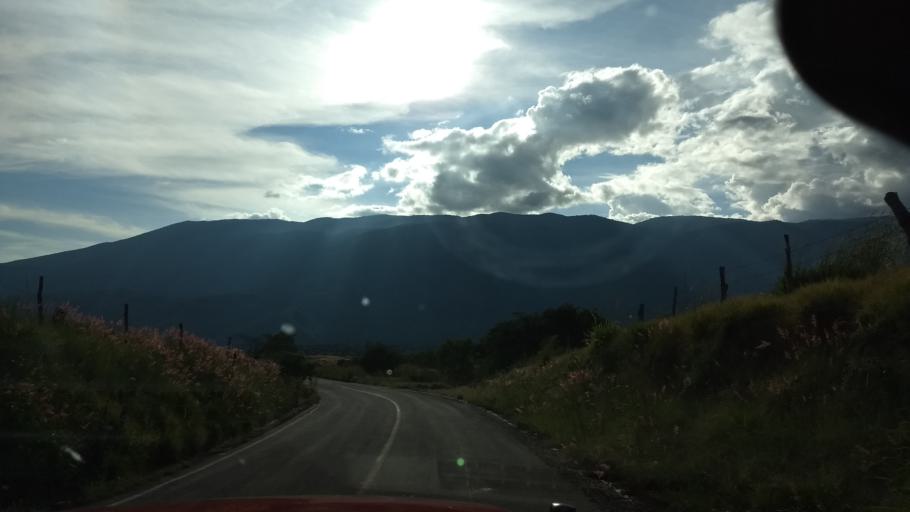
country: MX
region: Colima
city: Suchitlan
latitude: 19.4569
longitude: -103.8010
